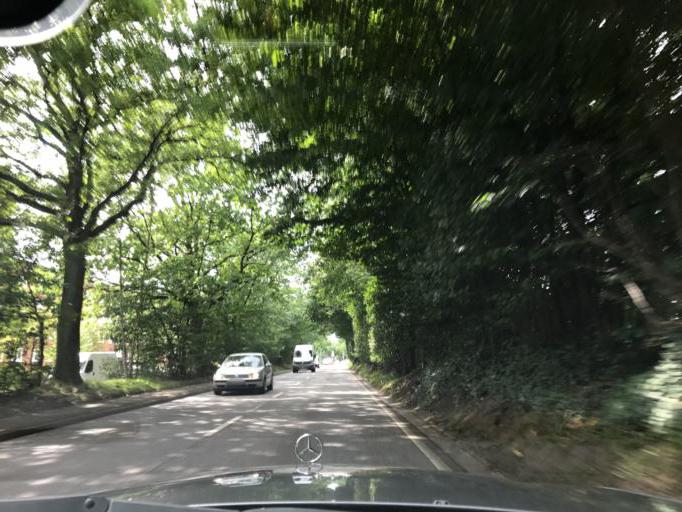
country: DE
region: Schleswig-Holstein
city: Glinde
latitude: 53.5116
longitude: 10.1893
